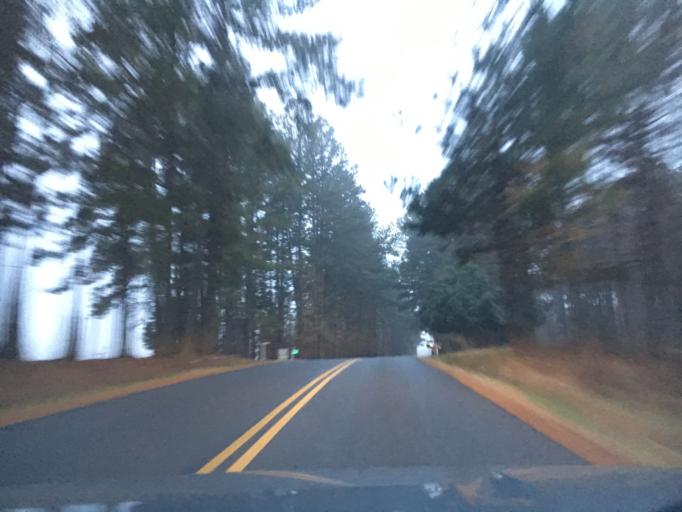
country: US
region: Virginia
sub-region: Halifax County
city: Mountain Road
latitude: 36.6836
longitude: -79.0053
